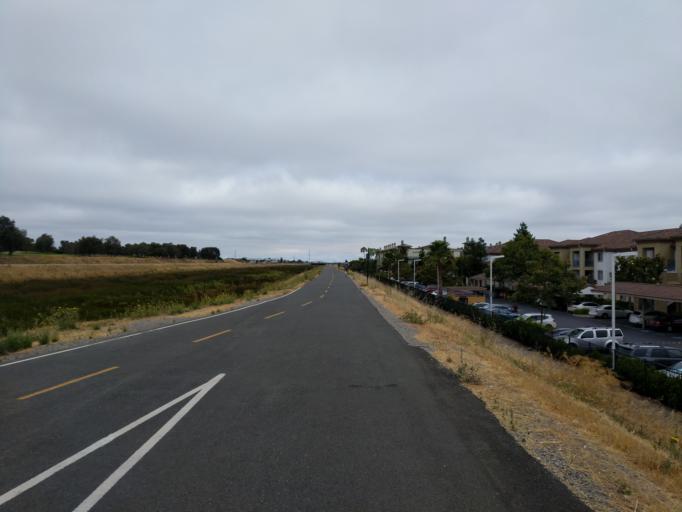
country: US
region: California
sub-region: Santa Clara County
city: Milpitas
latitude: 37.4111
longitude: -121.9610
